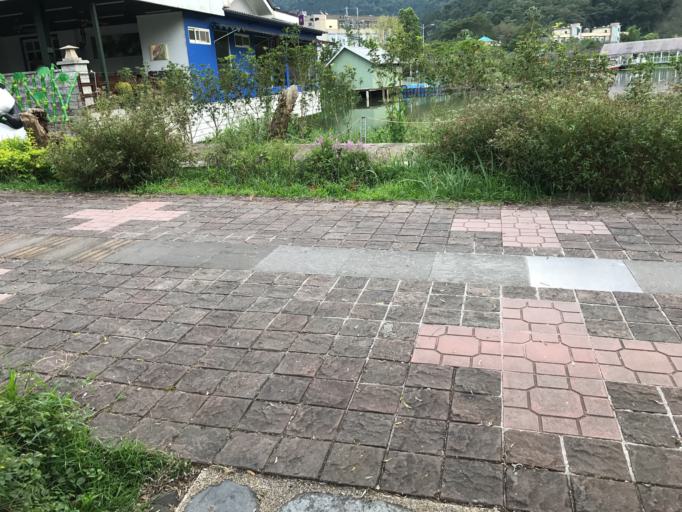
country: TW
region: Taiwan
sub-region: Nantou
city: Puli
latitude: 23.9609
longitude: 120.9993
